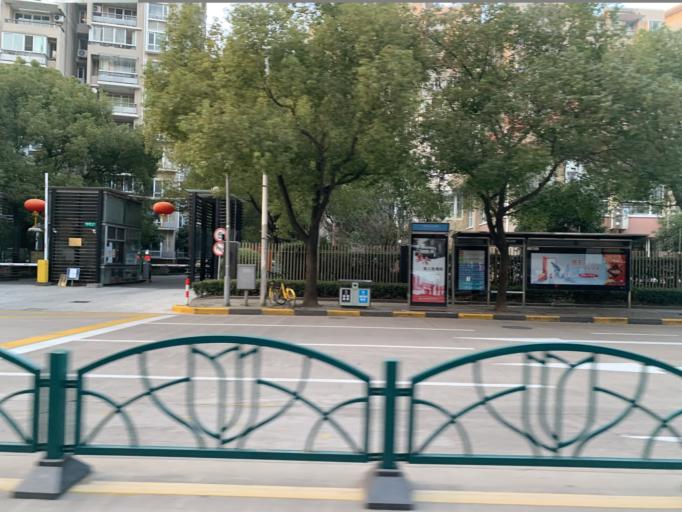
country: CN
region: Shanghai Shi
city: Huamu
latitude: 31.2285
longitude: 121.5481
